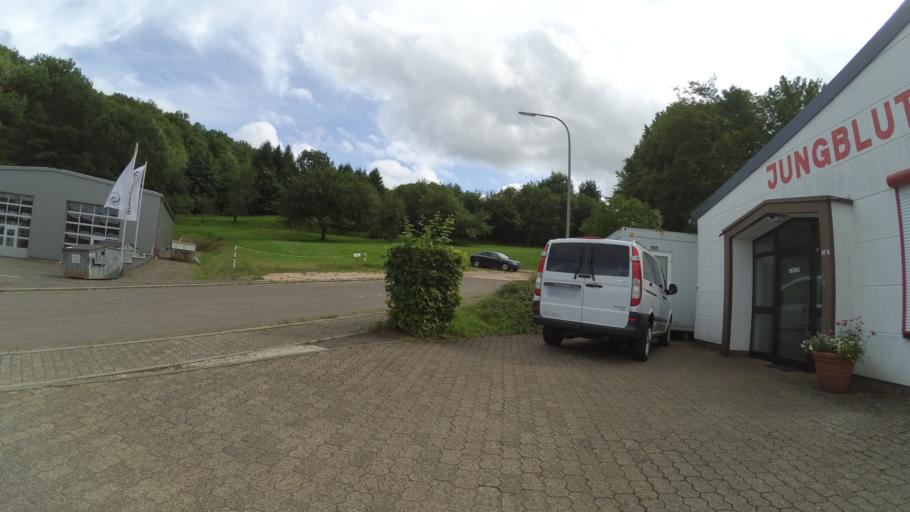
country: DE
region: Saarland
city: Tholey
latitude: 49.4865
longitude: 6.9838
